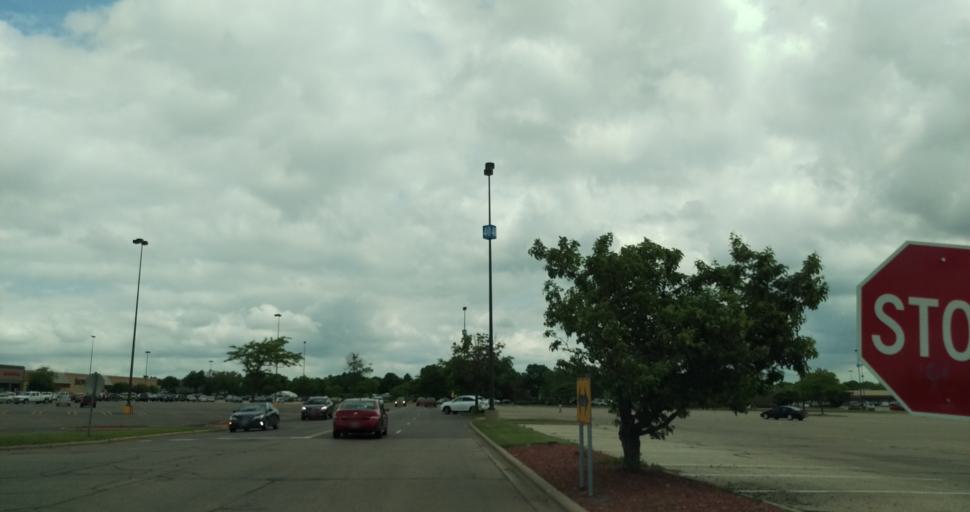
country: US
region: Wisconsin
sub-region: Dane County
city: Middleton
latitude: 43.0570
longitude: -89.5093
